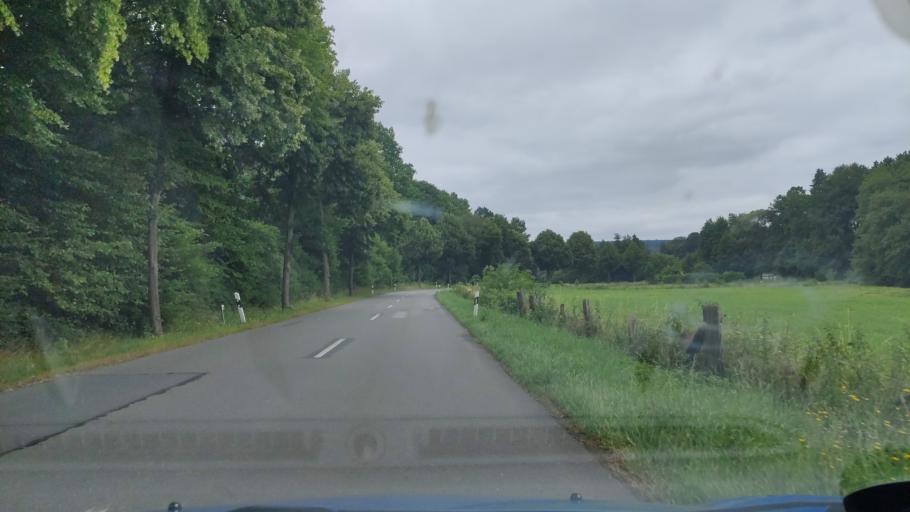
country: DE
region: Lower Saxony
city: Holzminden
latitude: 51.8187
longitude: 9.4743
